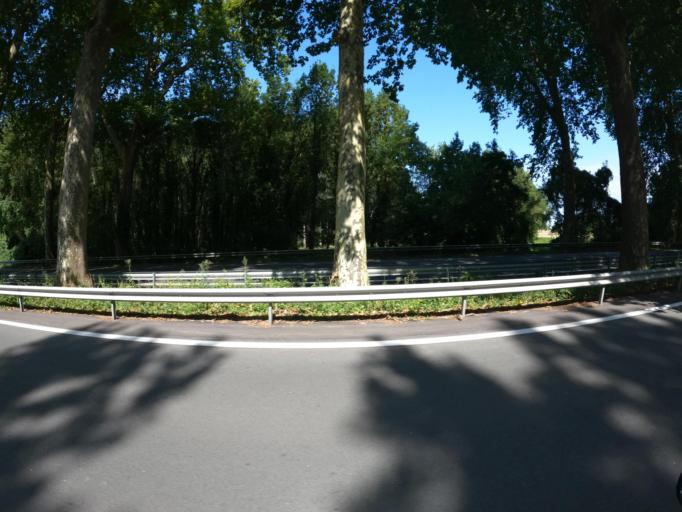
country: FR
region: Poitou-Charentes
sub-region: Departement des Deux-Sevres
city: Mauze-sur-le-Mignon
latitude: 46.2076
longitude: -0.6372
